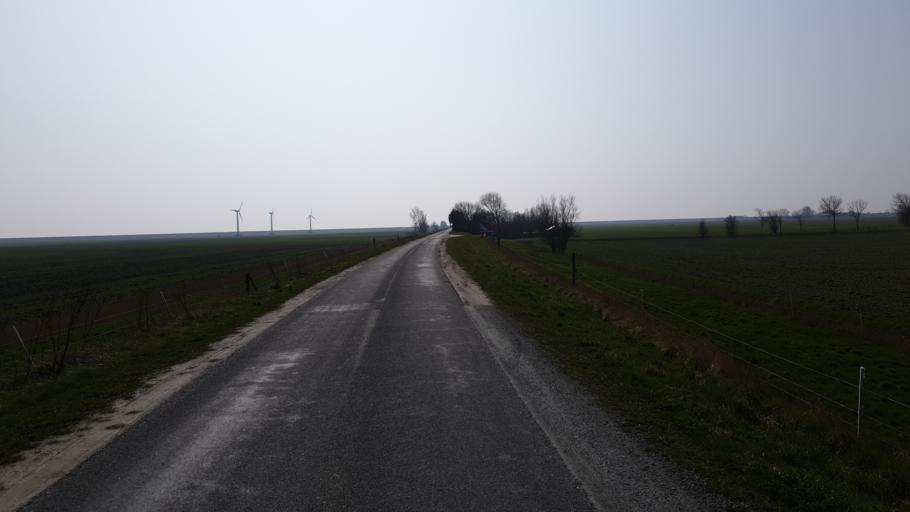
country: DE
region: Schleswig-Holstein
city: Elisabeth-Sophien-Koog
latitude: 54.4747
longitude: 8.8683
